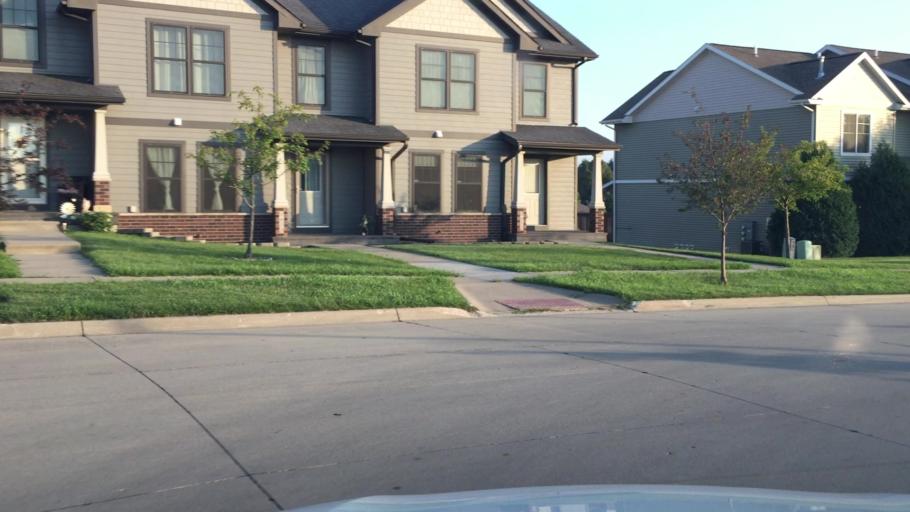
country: US
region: Iowa
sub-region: Johnson County
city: Iowa City
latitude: 41.6674
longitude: -91.4807
